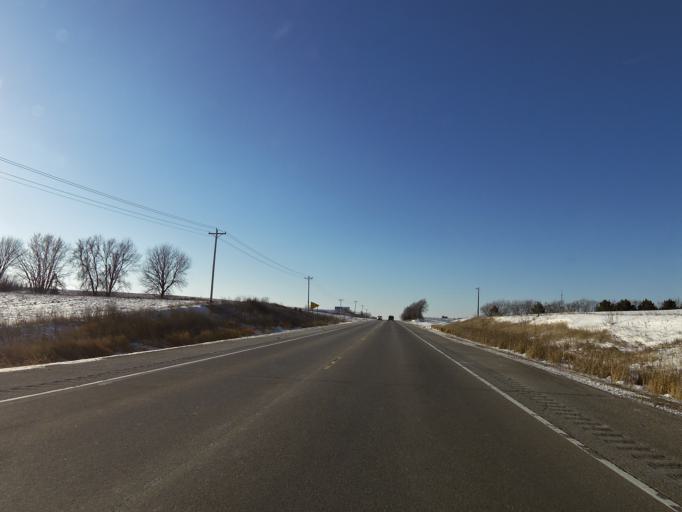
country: US
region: Minnesota
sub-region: Le Sueur County
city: New Prague
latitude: 44.5437
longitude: -93.5181
